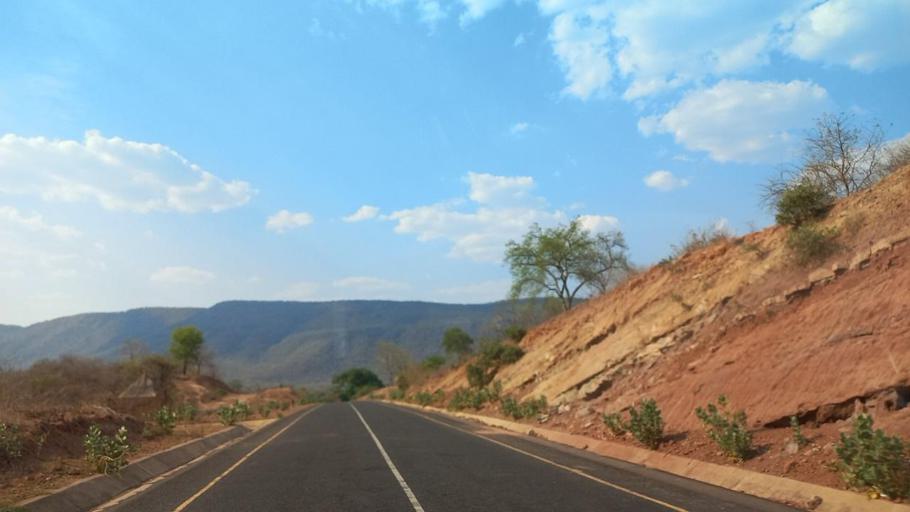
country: ZM
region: Lusaka
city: Luangwa
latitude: -15.0598
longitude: 30.2097
